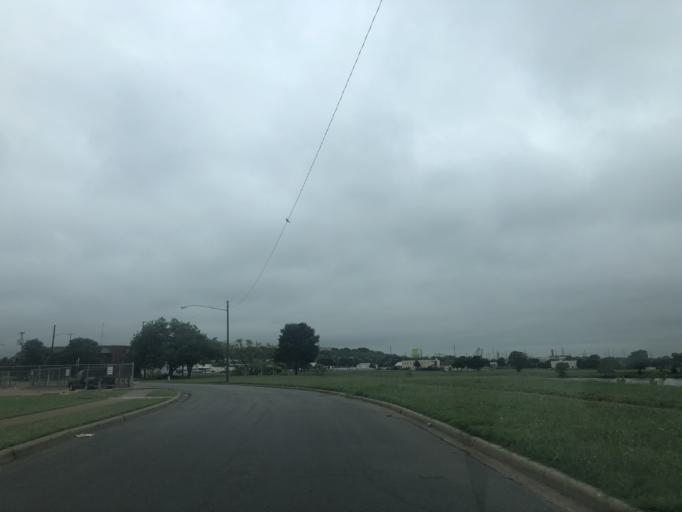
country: US
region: Texas
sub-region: Dallas County
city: Cockrell Hill
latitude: 32.7818
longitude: -96.8601
